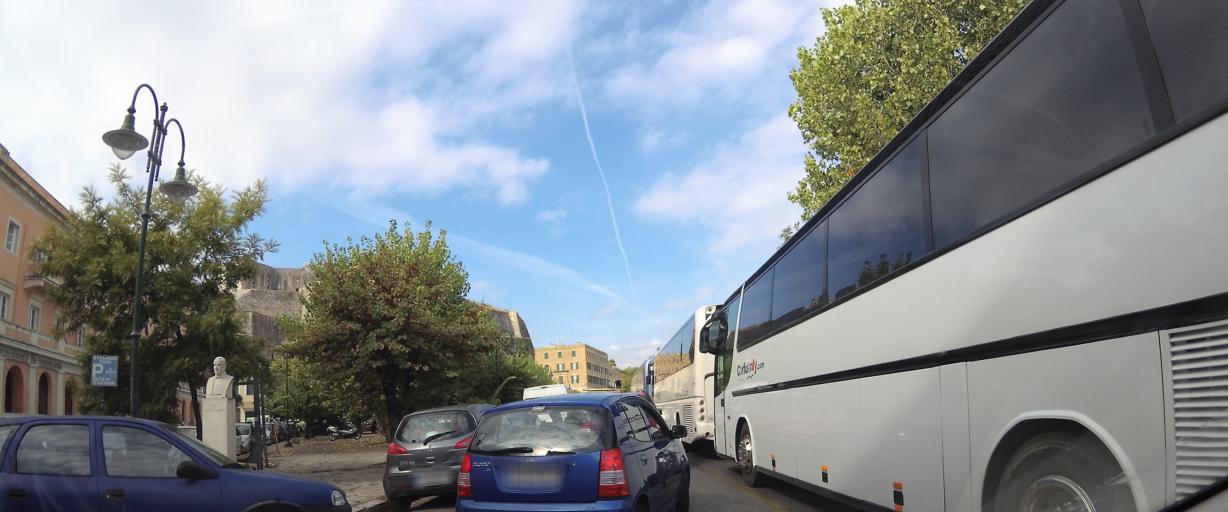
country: GR
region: Ionian Islands
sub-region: Nomos Kerkyras
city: Kerkyra
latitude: 39.6261
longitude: 19.9193
